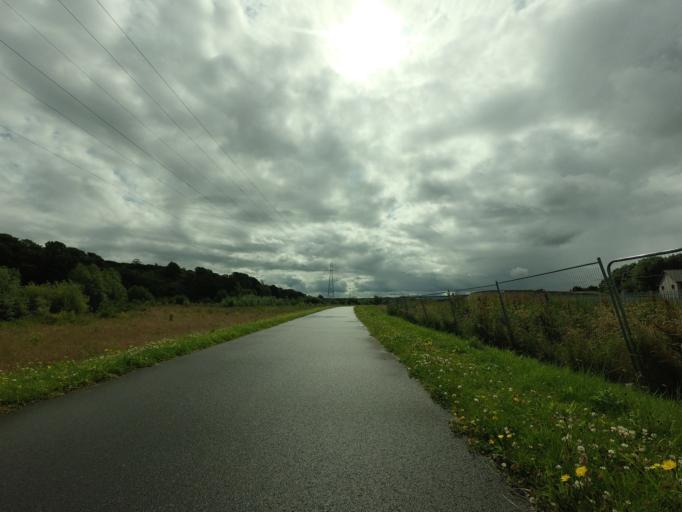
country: GB
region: Scotland
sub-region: Moray
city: Elgin
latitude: 57.6499
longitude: -3.2859
